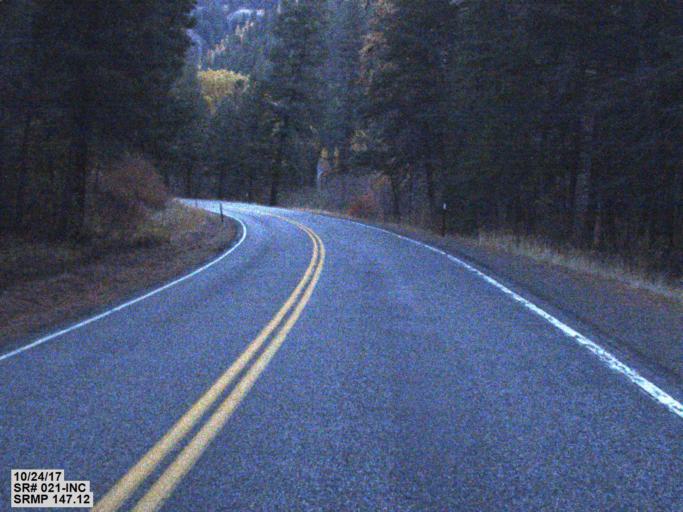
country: US
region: Washington
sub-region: Ferry County
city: Republic
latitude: 48.4731
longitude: -118.7380
